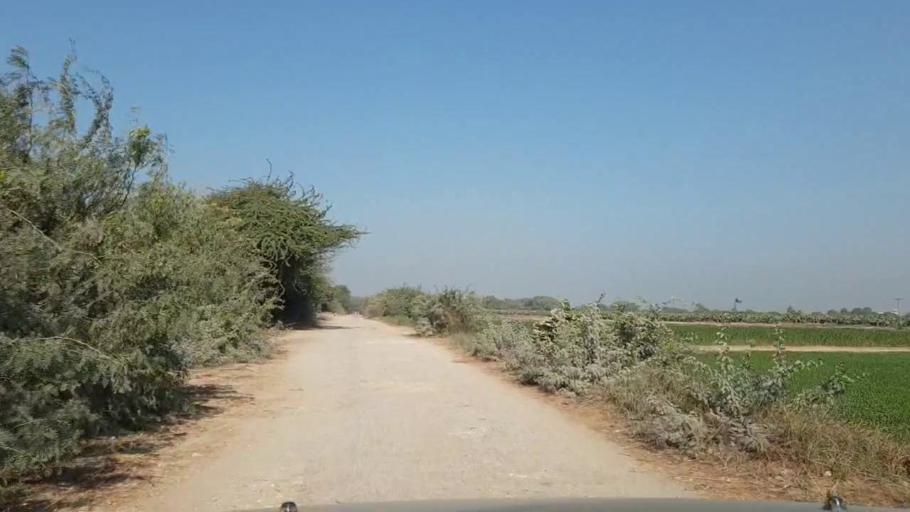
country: PK
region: Sindh
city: Matiari
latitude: 25.5828
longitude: 68.6025
